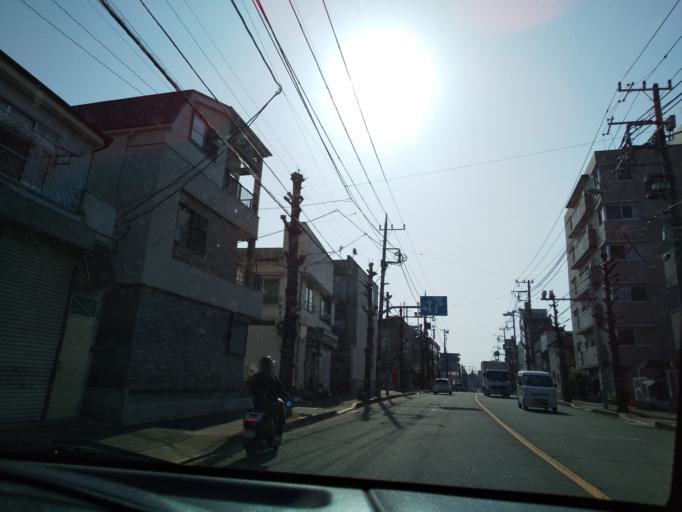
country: JP
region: Tokyo
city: Hino
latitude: 35.7061
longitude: 139.3804
